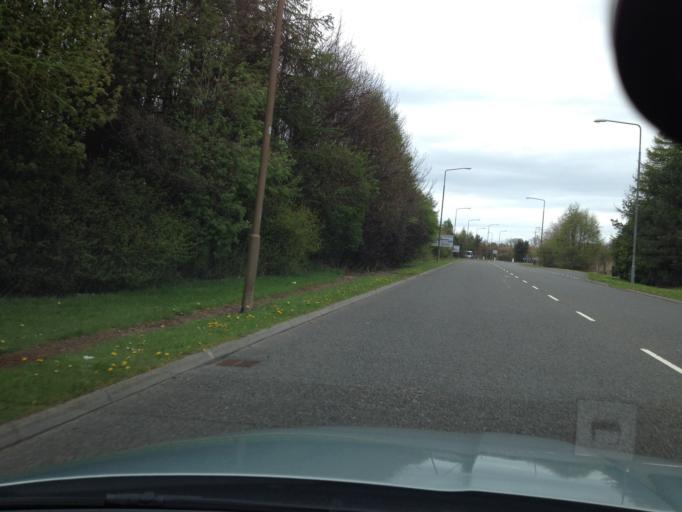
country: GB
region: Scotland
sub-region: West Lothian
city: Livingston
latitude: 55.8935
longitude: -3.5597
